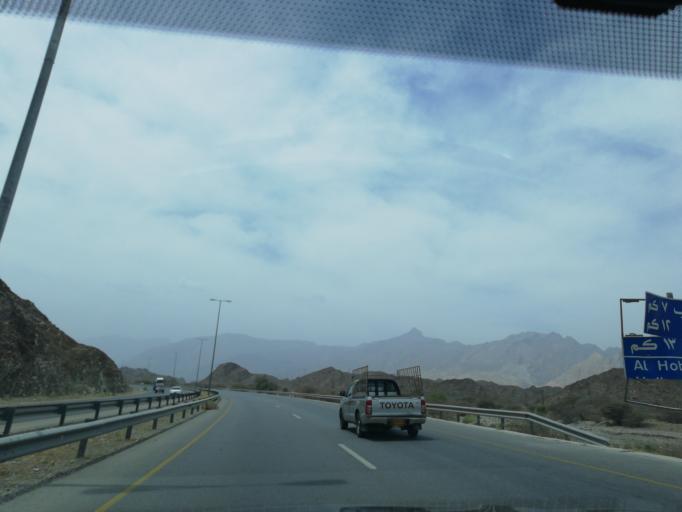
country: OM
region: Muhafazat ad Dakhiliyah
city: Sufalat Sama'il
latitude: 23.3443
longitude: 58.0017
